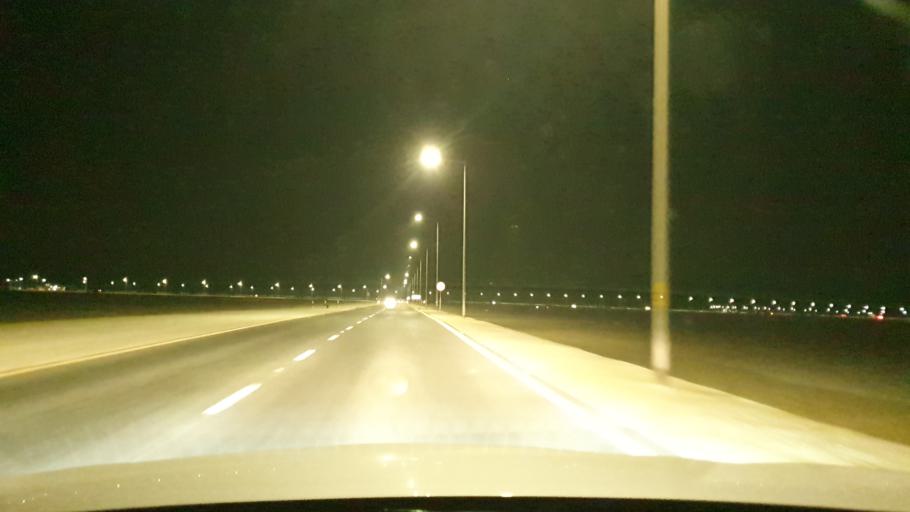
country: BH
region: Muharraq
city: Al Muharraq
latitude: 26.2837
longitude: 50.5836
